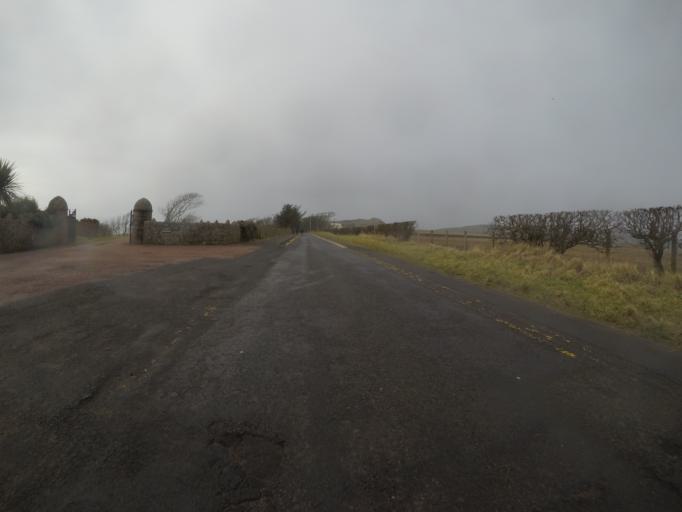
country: GB
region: Scotland
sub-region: North Ayrshire
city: West Kilbride
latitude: 55.6967
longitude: -4.8833
